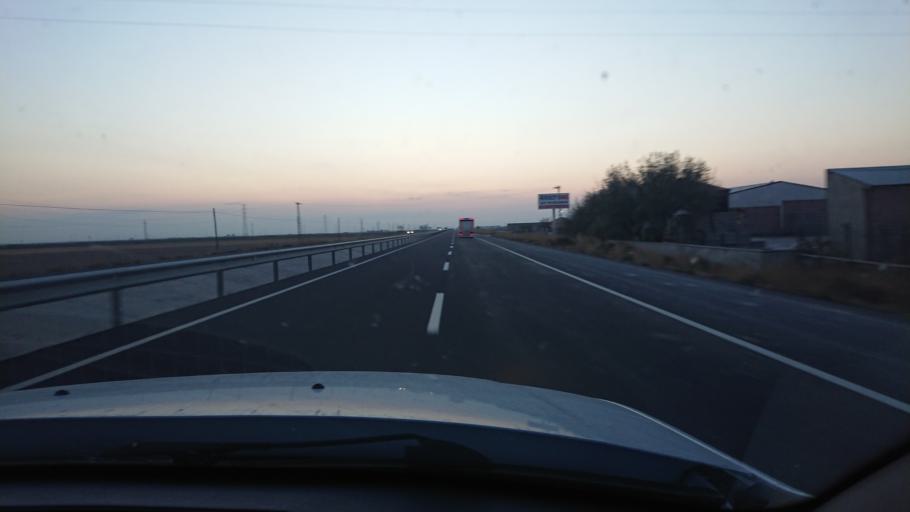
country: TR
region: Aksaray
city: Yesilova
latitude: 38.3145
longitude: 33.8447
